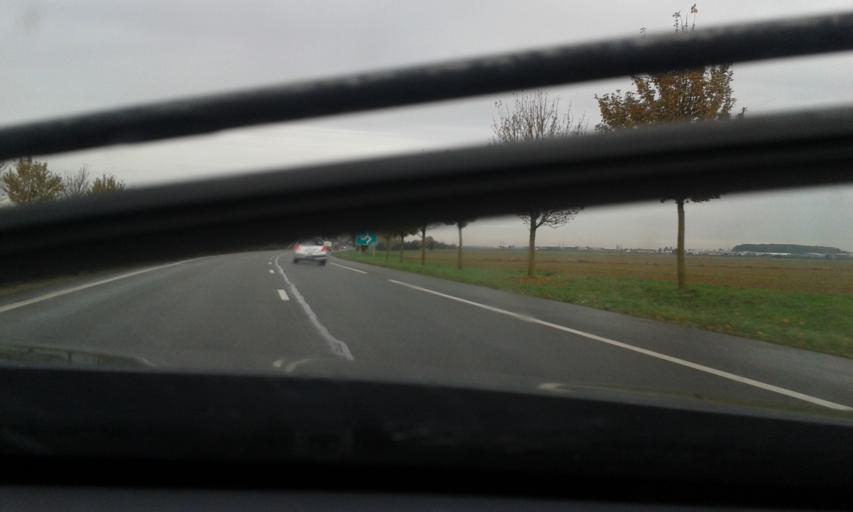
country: FR
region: Centre
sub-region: Departement d'Eure-et-Loir
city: Mainvilliers
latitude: 48.4319
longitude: 1.4313
